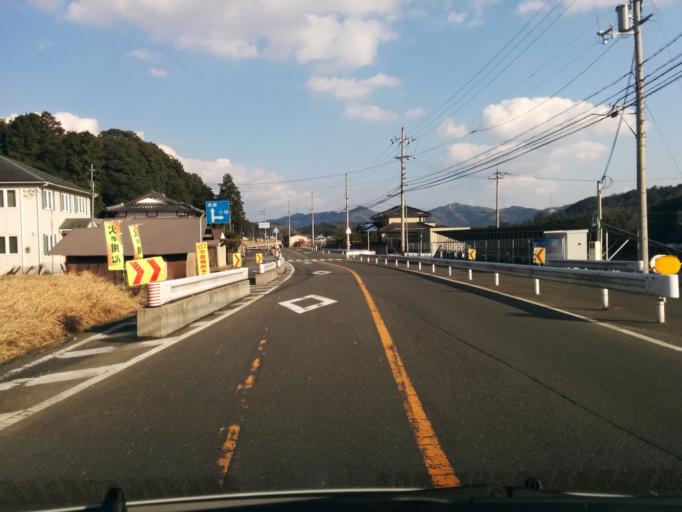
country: JP
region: Kyoto
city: Ayabe
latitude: 35.3636
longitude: 135.2048
